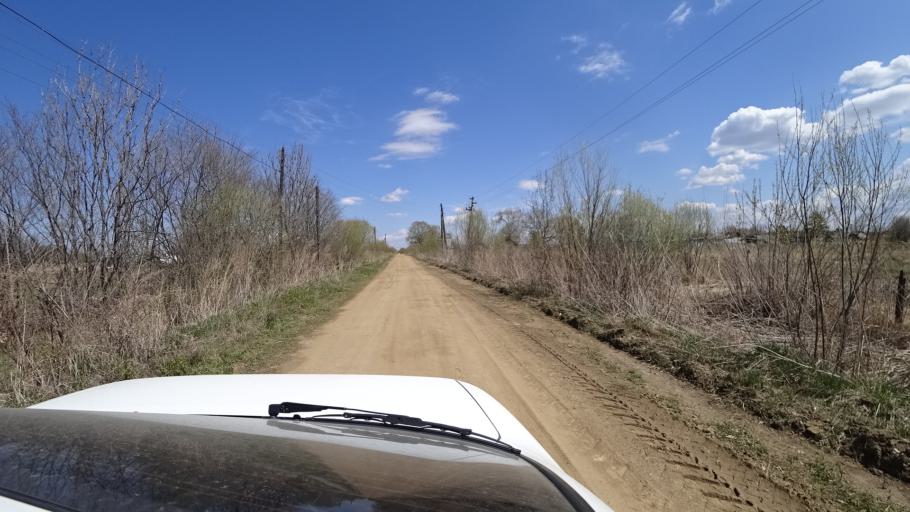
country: RU
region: Primorskiy
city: Dal'nerechensk
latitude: 45.7989
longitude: 133.7650
